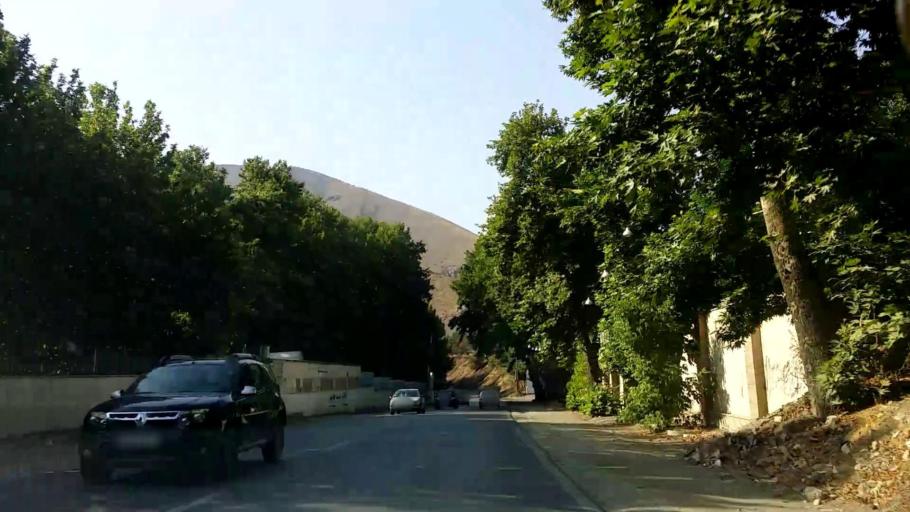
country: IR
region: Alborz
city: Karaj
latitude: 35.8550
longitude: 51.0590
